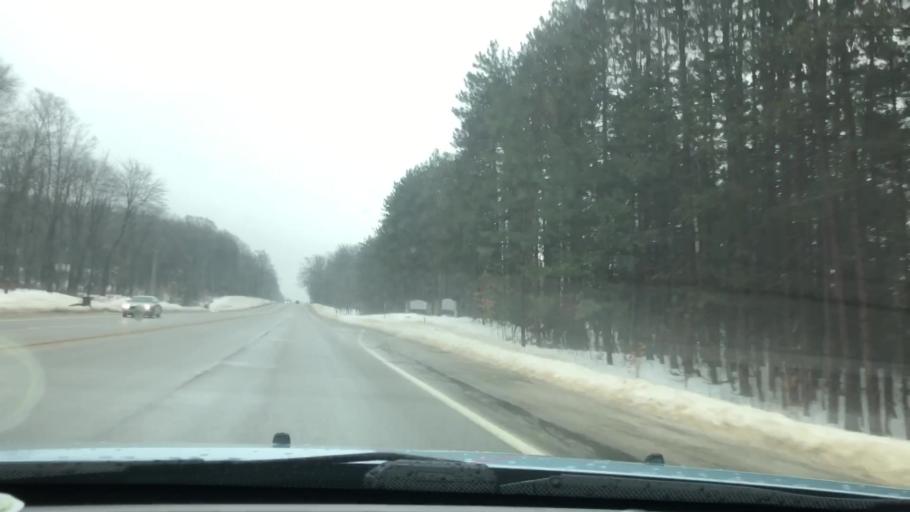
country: US
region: Michigan
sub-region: Otsego County
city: Gaylord
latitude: 45.0404
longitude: -84.7759
